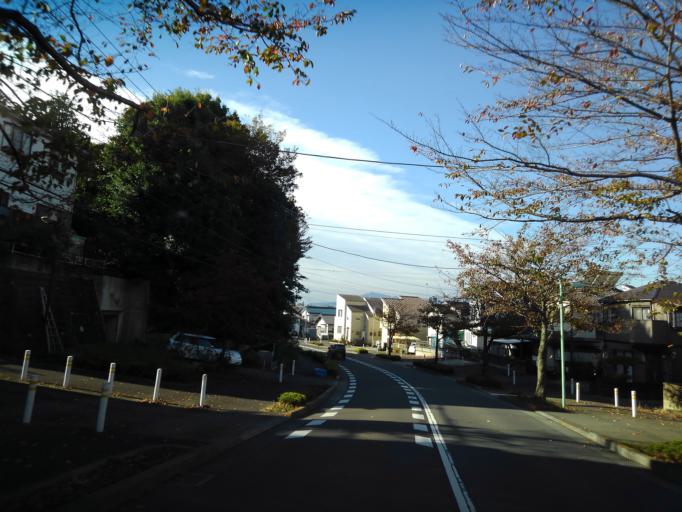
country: JP
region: Tokyo
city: Hino
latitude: 35.5933
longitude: 139.3875
